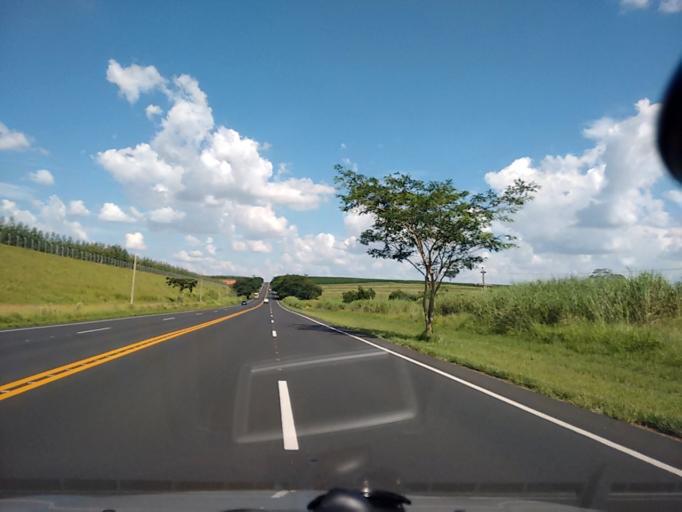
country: BR
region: Sao Paulo
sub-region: Pompeia
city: Pompeia
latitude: -22.1379
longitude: -50.1205
